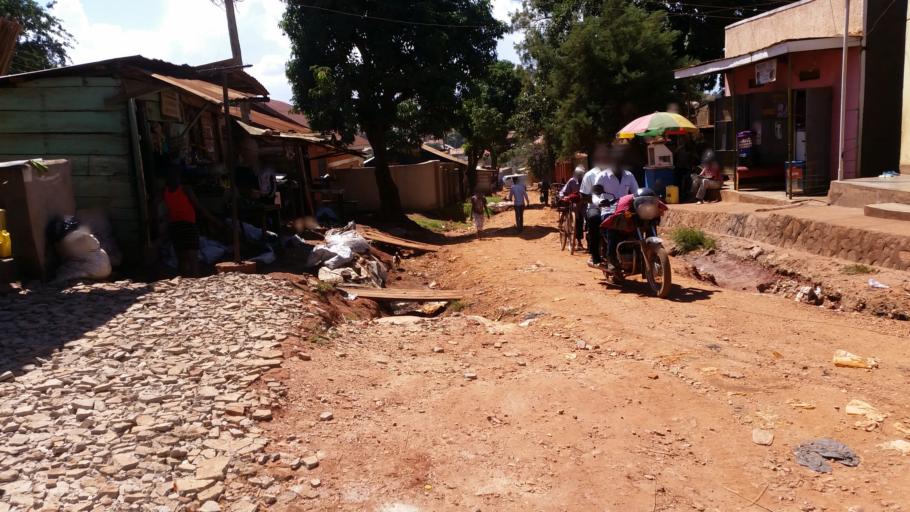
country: UG
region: Central Region
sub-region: Wakiso District
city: Kireka
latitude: 0.3428
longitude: 32.6473
